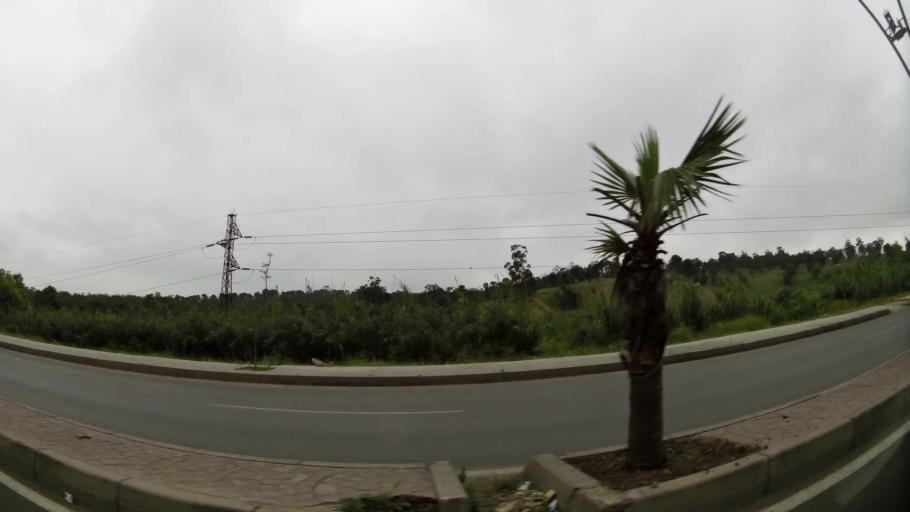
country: MA
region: Fes-Boulemane
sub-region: Fes
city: Fes
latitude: 34.0515
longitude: -4.9839
